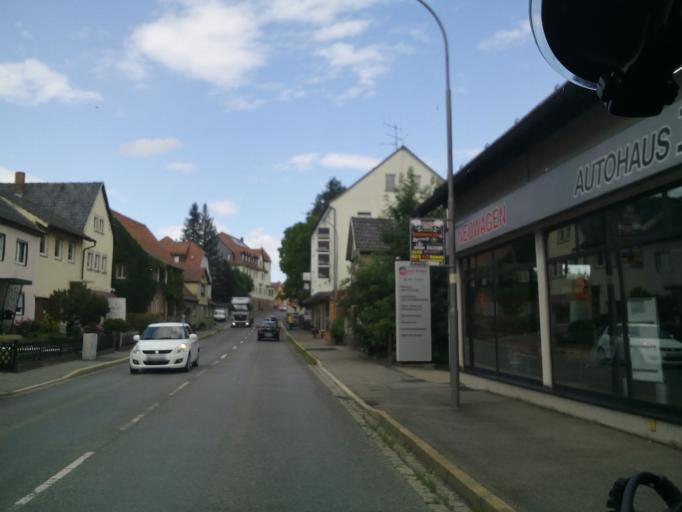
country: DE
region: Bavaria
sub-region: Upper Franconia
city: Rodental
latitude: 50.2893
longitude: 11.0306
